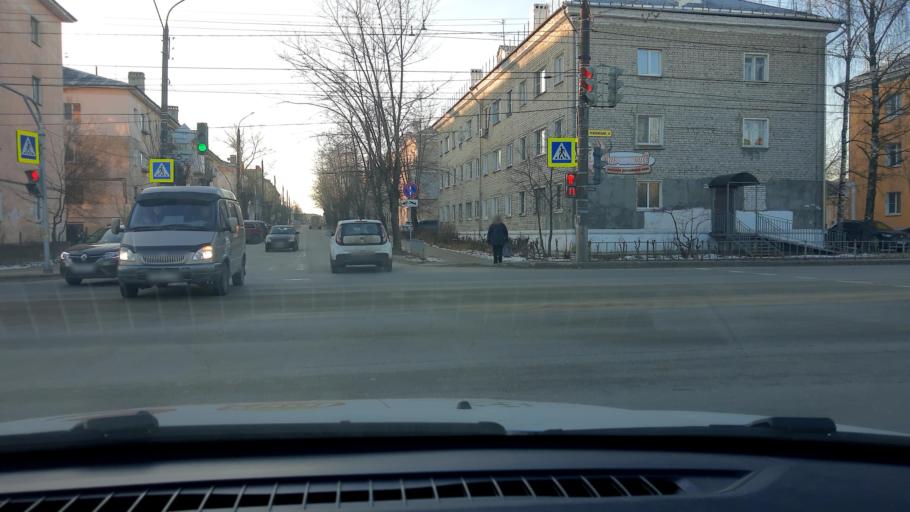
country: RU
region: Nizjnij Novgorod
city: Dzerzhinsk
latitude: 56.2492
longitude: 43.4569
